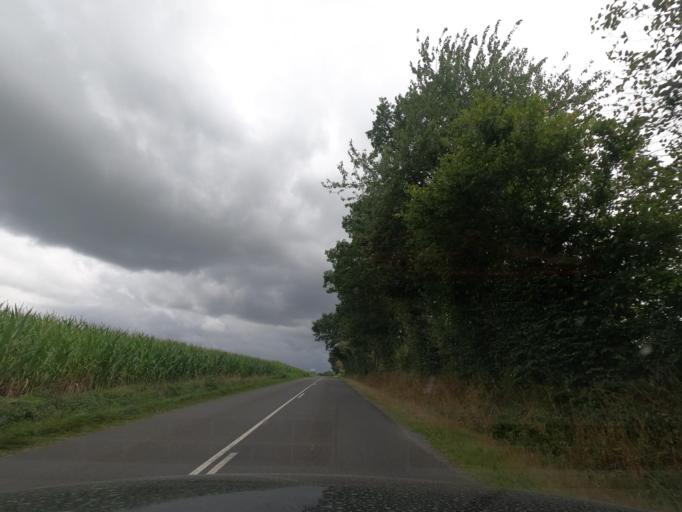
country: FR
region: Lower Normandy
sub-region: Departement de l'Orne
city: Briouze
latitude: 48.6923
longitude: -0.4109
